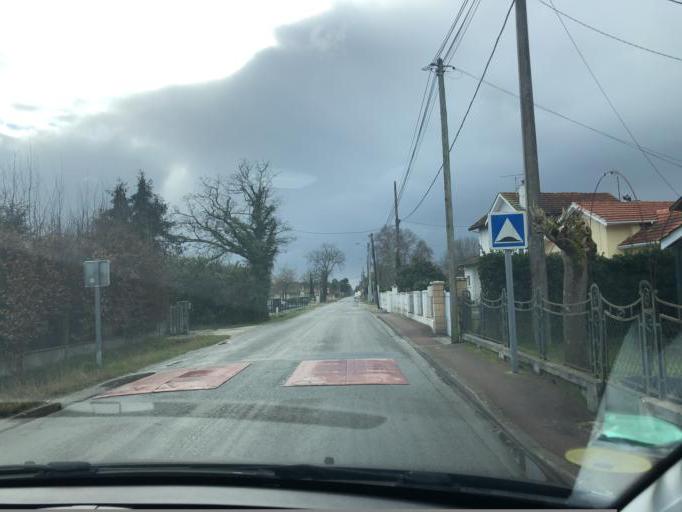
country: FR
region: Aquitaine
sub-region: Departement de la Gironde
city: Hourtin
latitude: 45.1829
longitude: -1.0603
